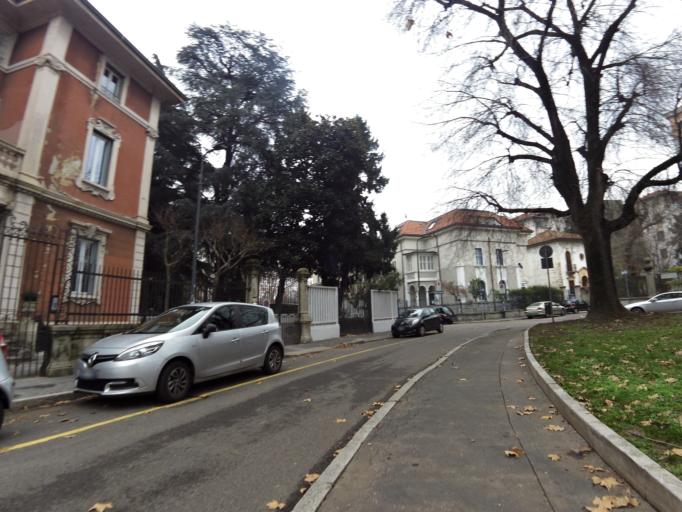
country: IT
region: Lombardy
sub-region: Citta metropolitana di Milano
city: Milano
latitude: 45.4465
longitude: 9.1862
